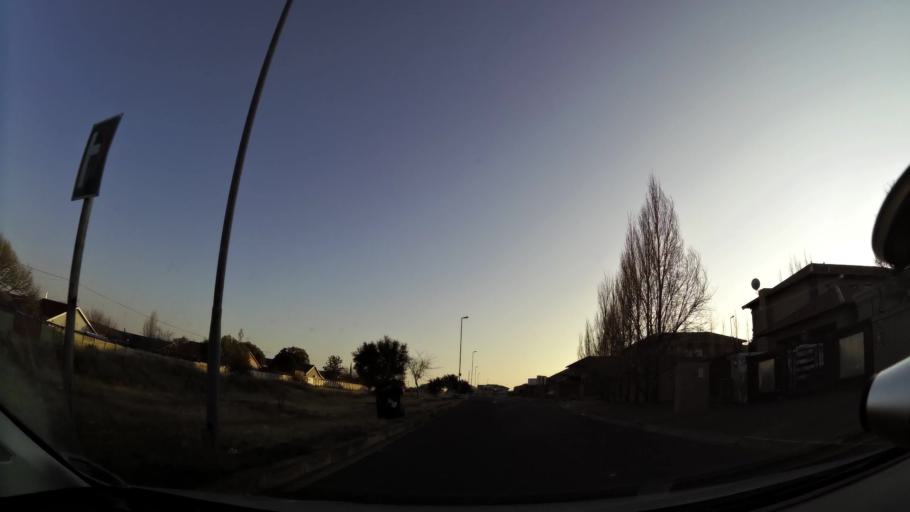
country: ZA
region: Orange Free State
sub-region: Mangaung Metropolitan Municipality
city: Bloemfontein
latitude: -29.0972
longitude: 26.1640
